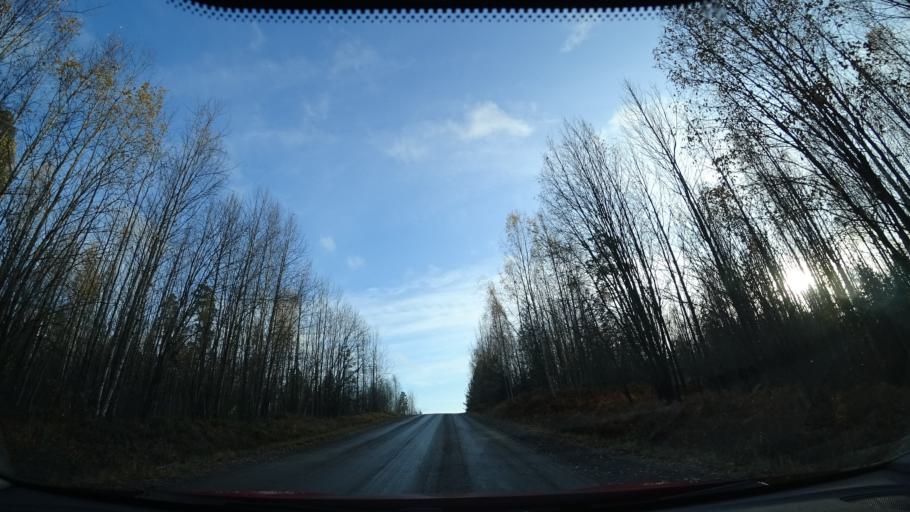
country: FI
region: Uusimaa
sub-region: Helsinki
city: Sibbo
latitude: 60.2990
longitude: 25.1993
